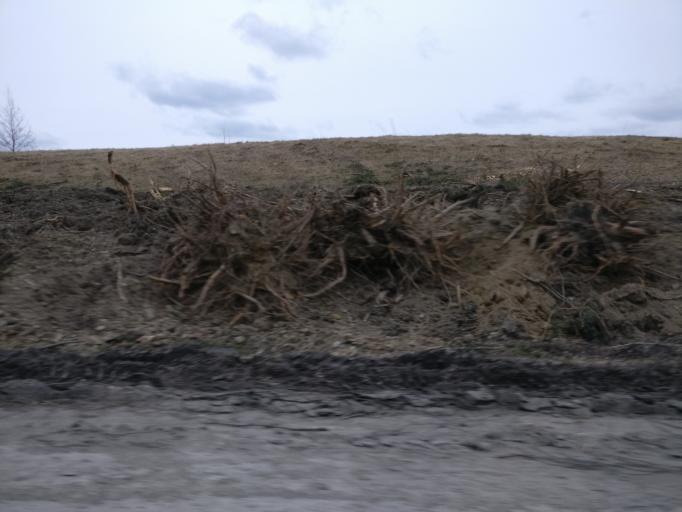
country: FI
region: Pirkanmaa
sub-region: Tampere
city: Tampere
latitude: 61.4757
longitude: 23.8355
